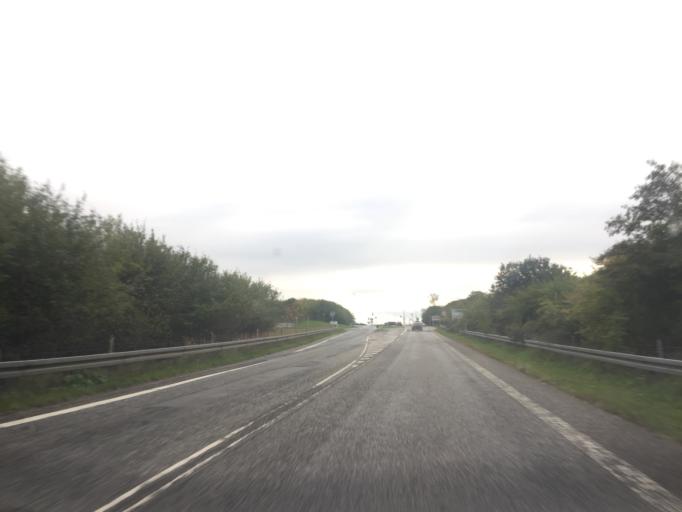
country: DK
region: Capital Region
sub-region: Egedal Kommune
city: Smorumnedre
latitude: 55.7569
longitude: 12.2899
